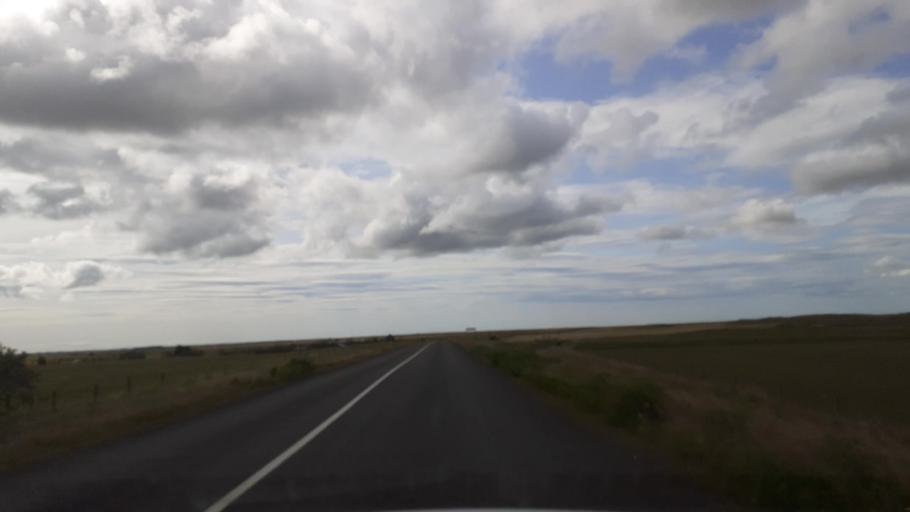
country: IS
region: South
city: Vestmannaeyjar
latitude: 63.8365
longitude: -20.4157
